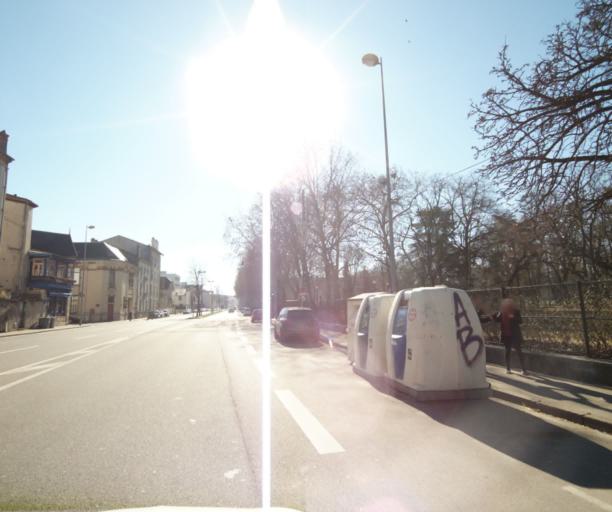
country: FR
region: Lorraine
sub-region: Departement de Meurthe-et-Moselle
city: Malzeville
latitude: 48.6992
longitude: 6.1874
